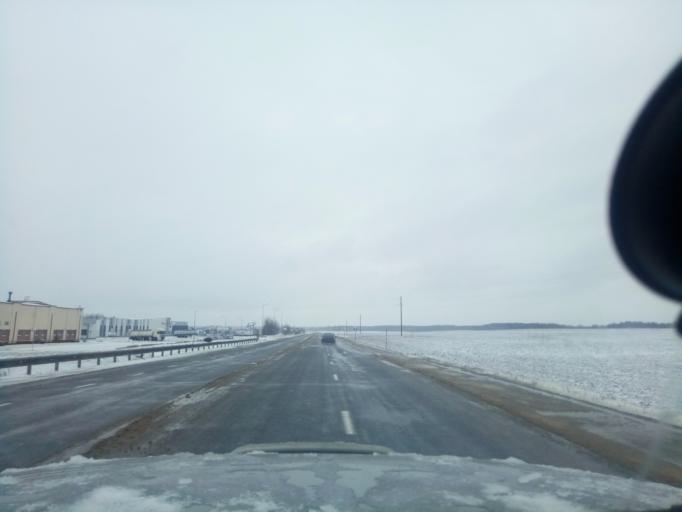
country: BY
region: Minsk
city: Nyasvizh
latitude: 53.2285
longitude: 26.6422
